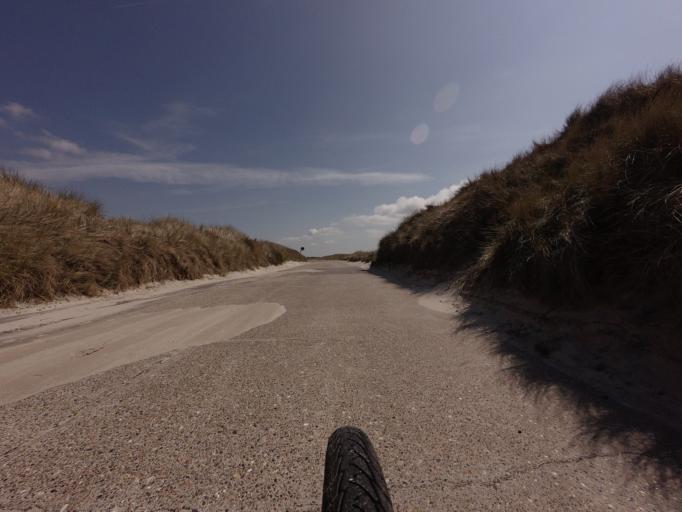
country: DK
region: North Denmark
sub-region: Jammerbugt Kommune
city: Brovst
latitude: 57.1776
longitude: 9.4373
